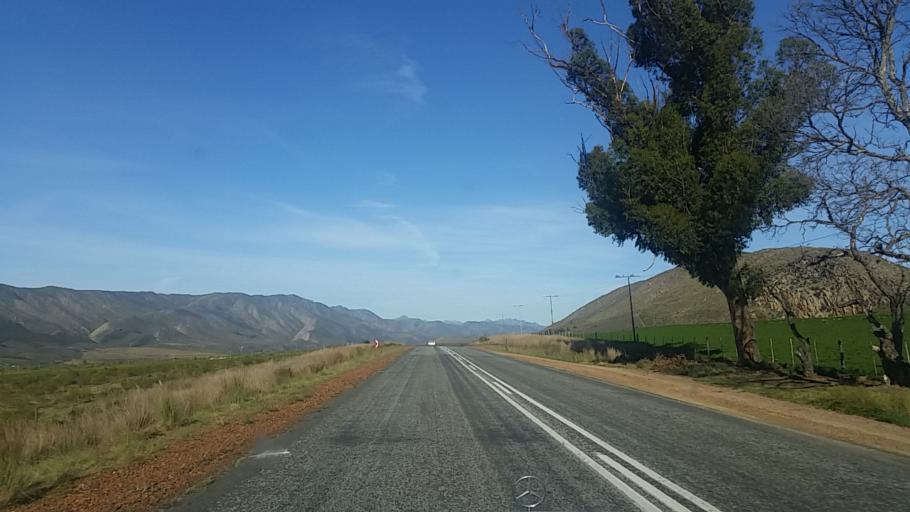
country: ZA
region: Western Cape
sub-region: Eden District Municipality
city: Knysna
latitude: -33.7724
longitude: 22.9448
